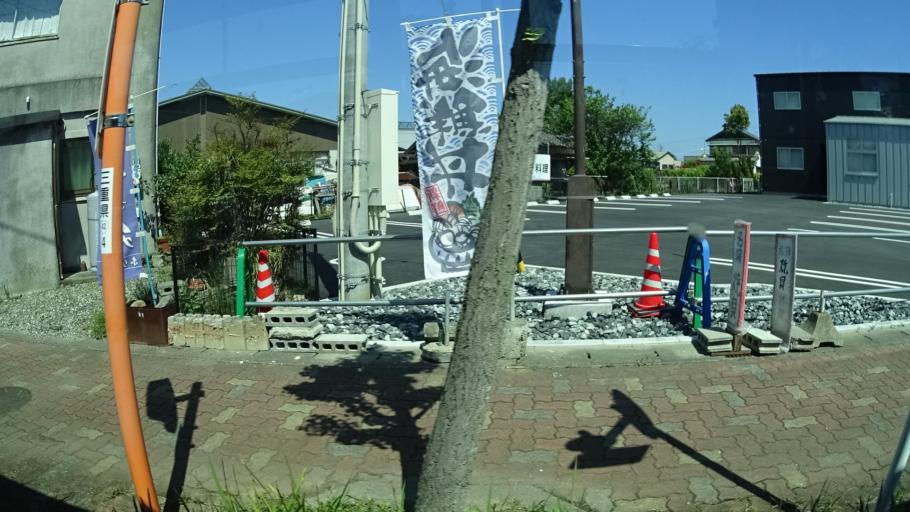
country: JP
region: Mie
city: Toba
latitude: 34.5052
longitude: 136.7784
